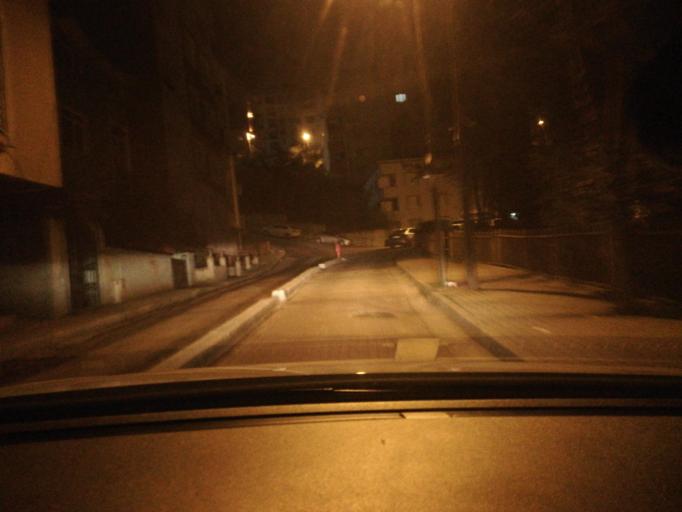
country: TR
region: Istanbul
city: Sisli
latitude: 41.0874
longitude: 28.9713
